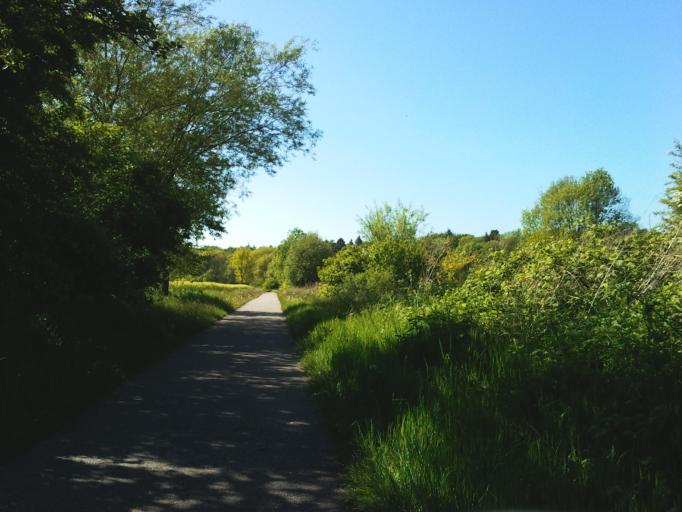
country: DE
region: Mecklenburg-Vorpommern
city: Nienhagen
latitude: 54.1533
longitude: 12.1859
